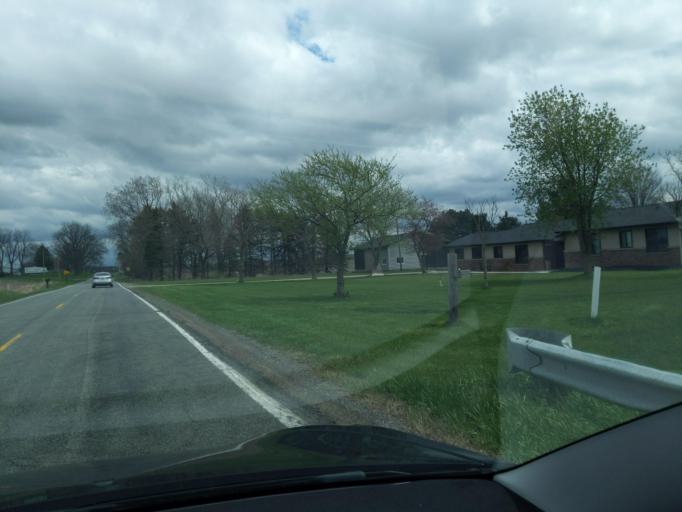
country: US
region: Michigan
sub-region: Ingham County
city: Mason
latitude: 42.5614
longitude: -84.4726
